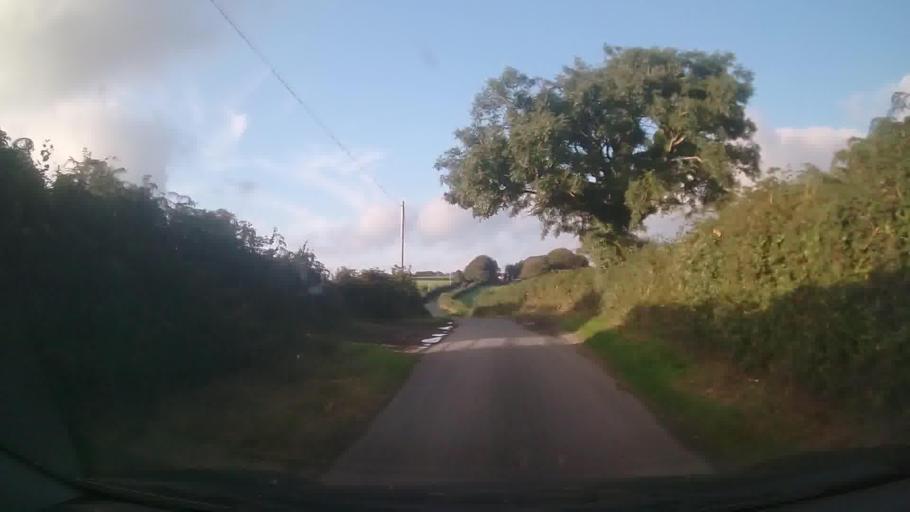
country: GB
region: Wales
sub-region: Pembrokeshire
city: Saundersfoot
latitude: 51.7438
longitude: -4.6595
